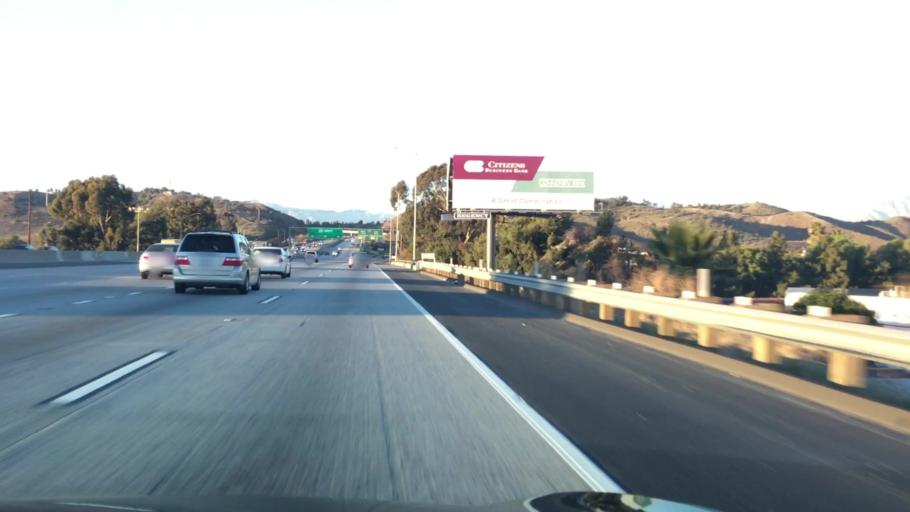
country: US
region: California
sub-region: Los Angeles County
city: Diamond Bar
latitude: 34.0557
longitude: -117.8034
